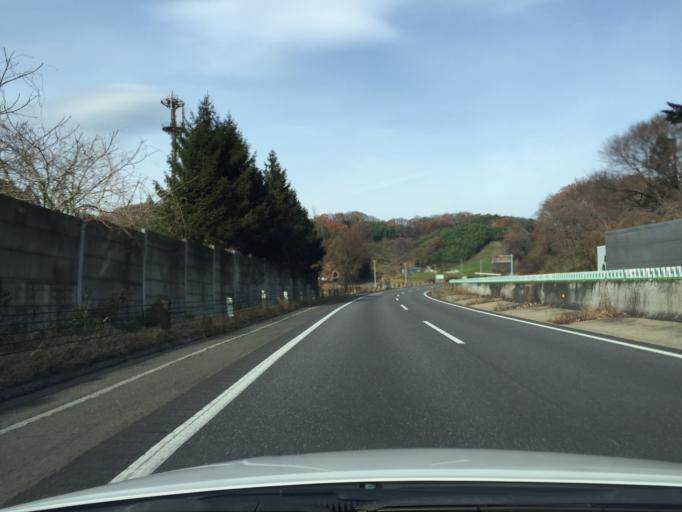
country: JP
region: Fukushima
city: Nihommatsu
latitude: 37.5945
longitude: 140.4185
